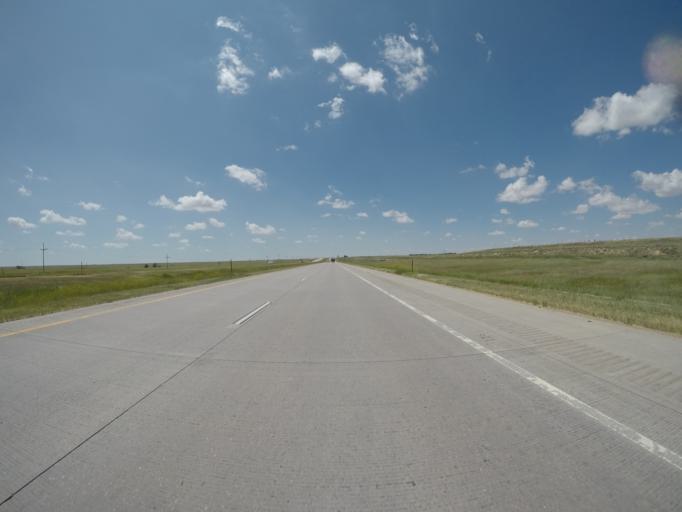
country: US
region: Colorado
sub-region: Lincoln County
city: Hugo
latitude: 39.2770
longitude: -103.0156
